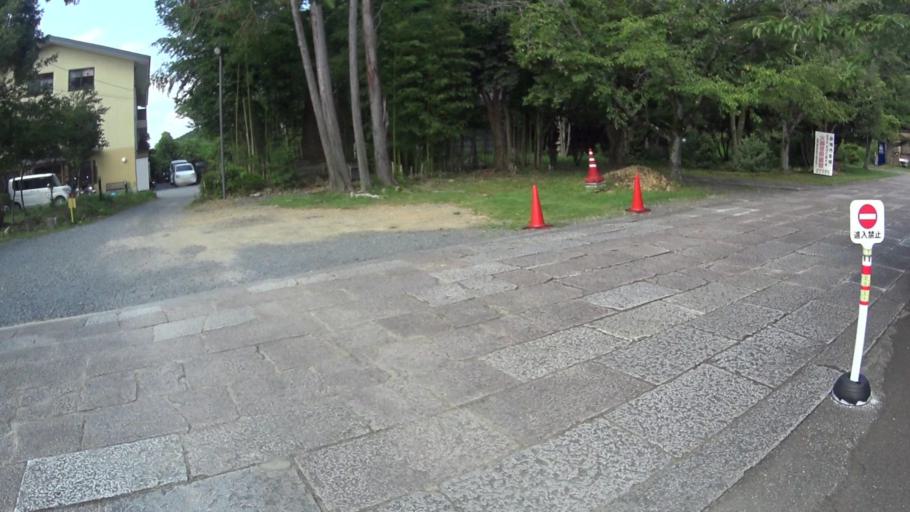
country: RU
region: Rostov
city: Remontnoye
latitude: 46.5012
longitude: 43.7608
